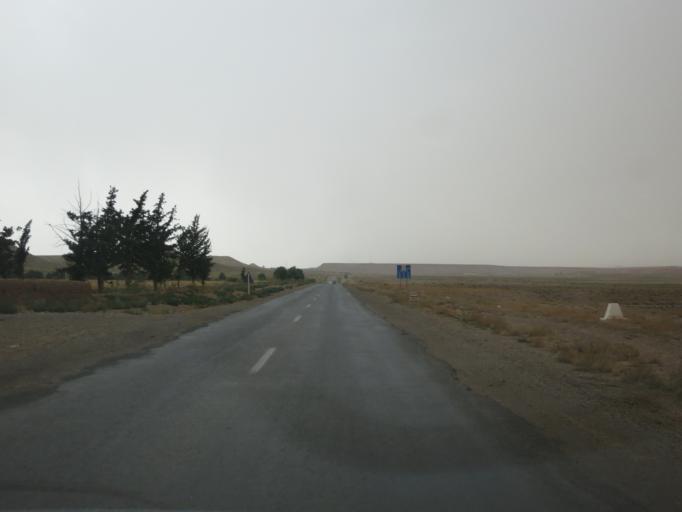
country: MA
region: Meknes-Tafilalet
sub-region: Khenifra
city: Midelt
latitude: 32.6793
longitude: -4.6718
